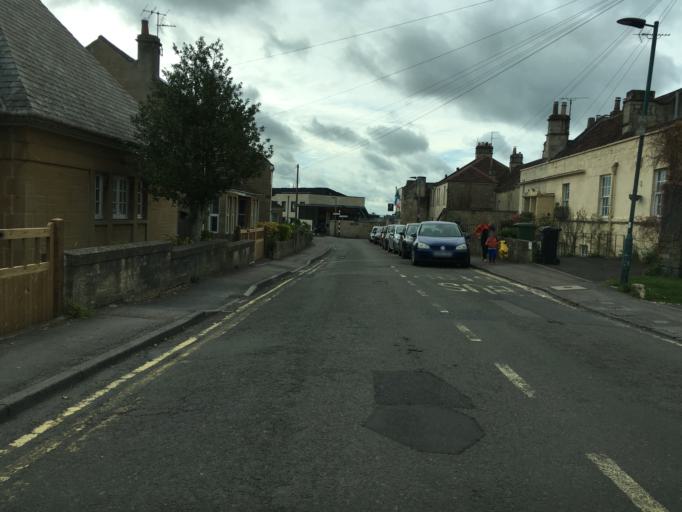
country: GB
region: England
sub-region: Bath and North East Somerset
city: Bath
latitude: 51.3593
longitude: -2.3507
